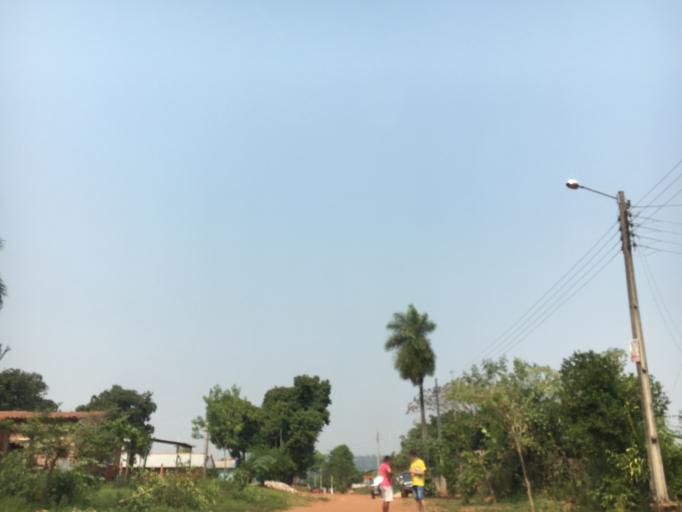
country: PY
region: Central
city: Nemby
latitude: -25.3878
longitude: -57.5664
